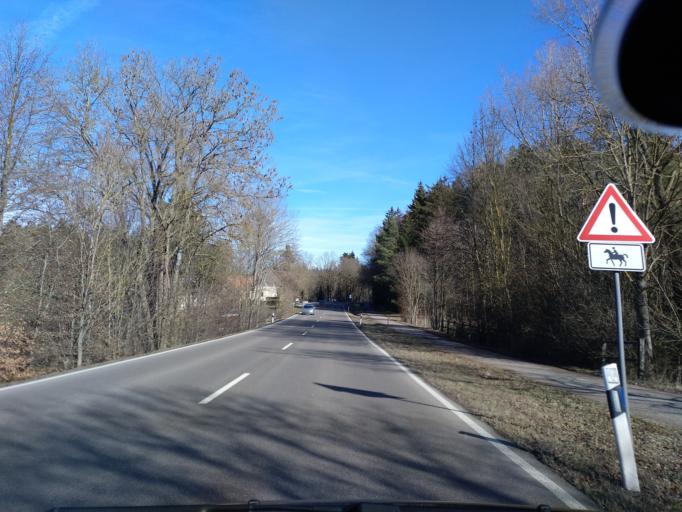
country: DE
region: Baden-Wuerttemberg
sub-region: Regierungsbezirk Stuttgart
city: Mainhardt
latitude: 49.0796
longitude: 9.5850
